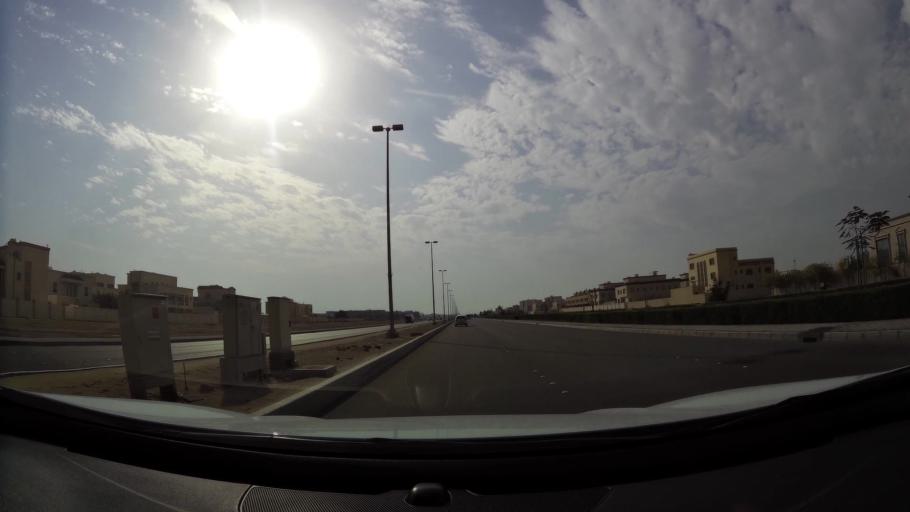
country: AE
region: Abu Dhabi
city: Abu Dhabi
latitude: 24.3482
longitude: 54.5626
